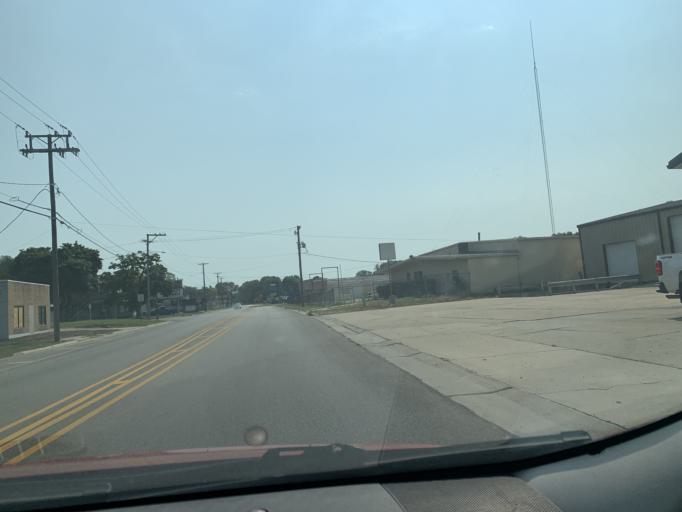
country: US
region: Illinois
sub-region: Whiteside County
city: Sterling
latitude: 41.7903
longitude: -89.7169
